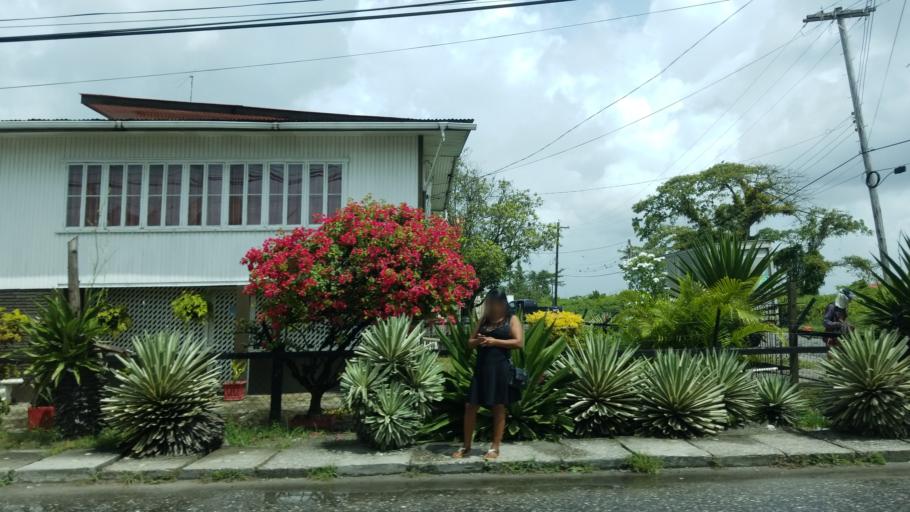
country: GY
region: Demerara-Mahaica
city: Georgetown
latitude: 6.7826
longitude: -58.1698
